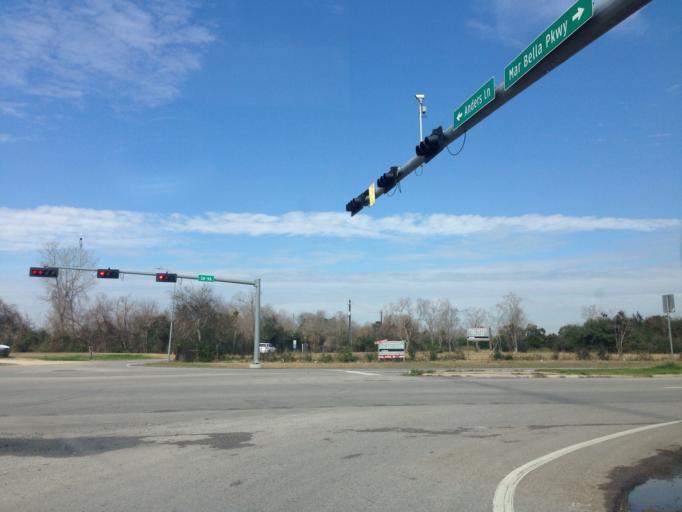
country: US
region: Texas
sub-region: Galveston County
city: Kemah
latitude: 29.5186
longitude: -95.0226
